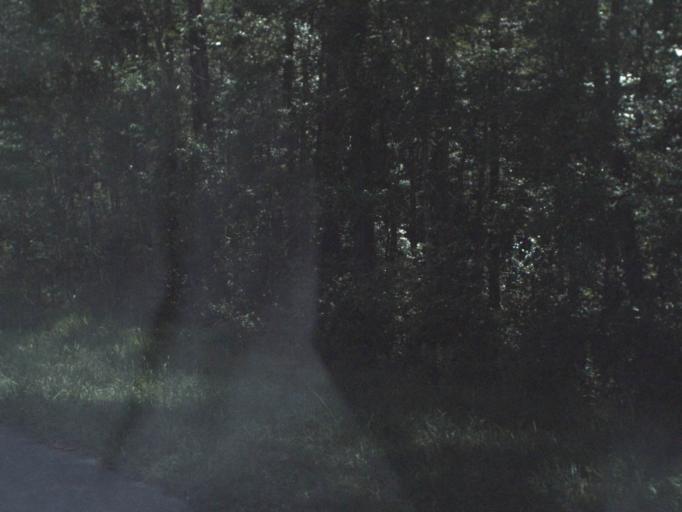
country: US
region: Florida
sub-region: Hamilton County
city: Jasper
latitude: 30.5272
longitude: -82.6746
